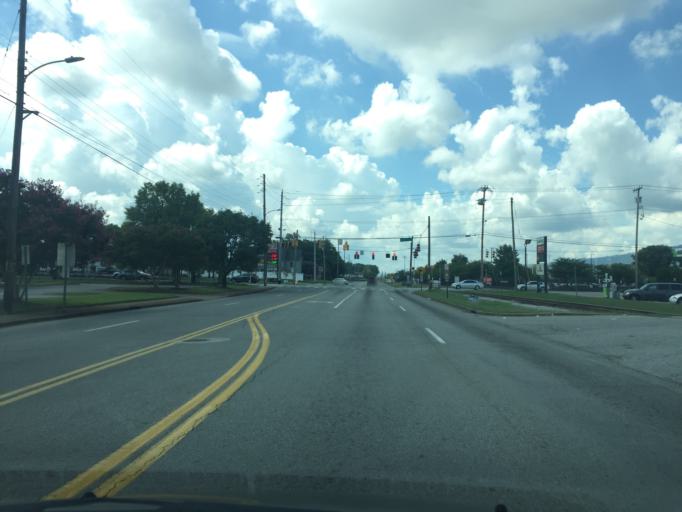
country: US
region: Tennessee
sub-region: Hamilton County
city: Chattanooga
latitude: 35.0445
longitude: -85.2796
